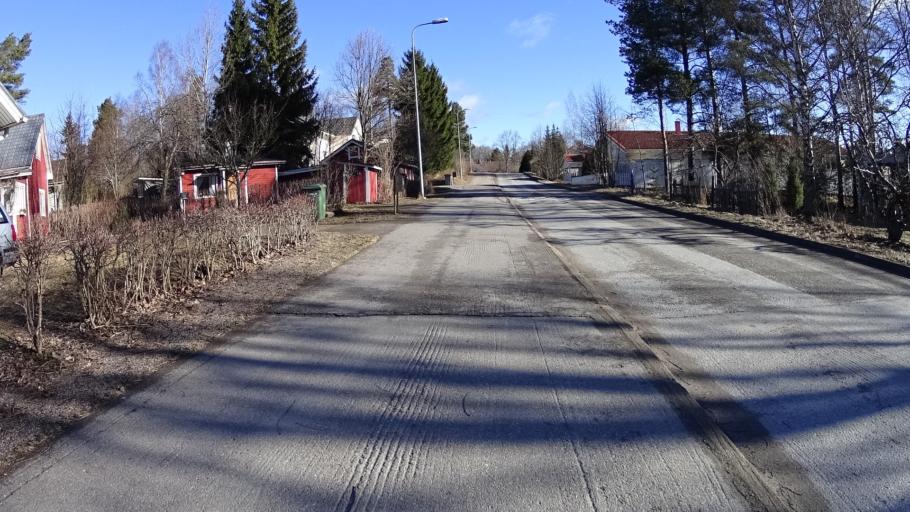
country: FI
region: Uusimaa
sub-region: Helsinki
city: Kilo
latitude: 60.2587
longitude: 24.7656
